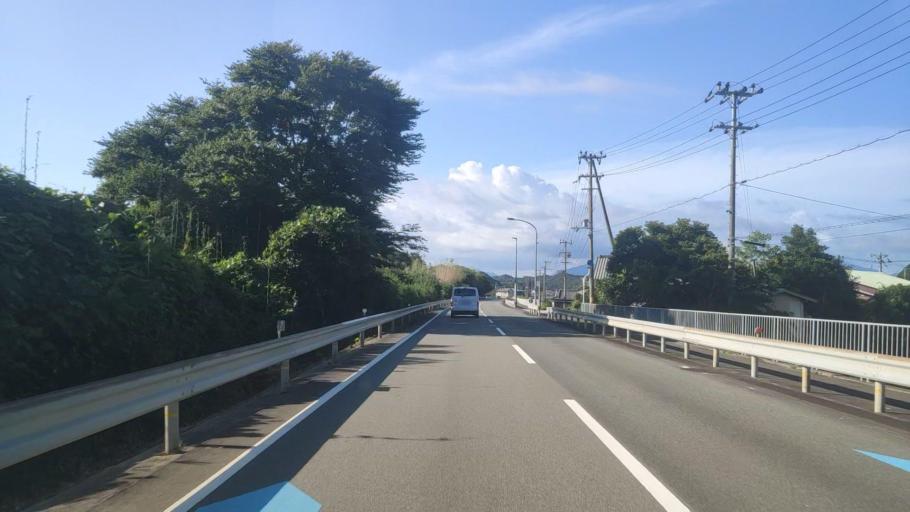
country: JP
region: Wakayama
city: Tanabe
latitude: 33.6715
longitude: 135.4079
